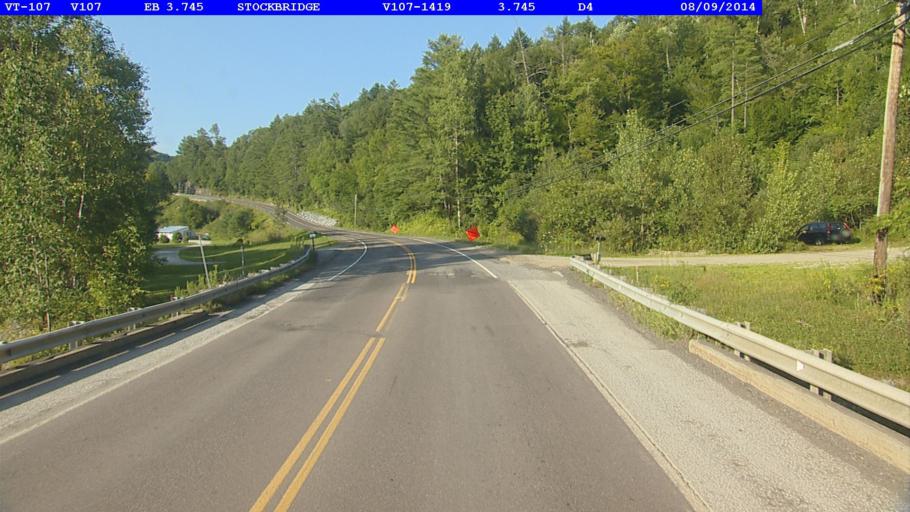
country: US
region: Vermont
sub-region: Orange County
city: Randolph
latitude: 43.7701
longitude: -72.7047
